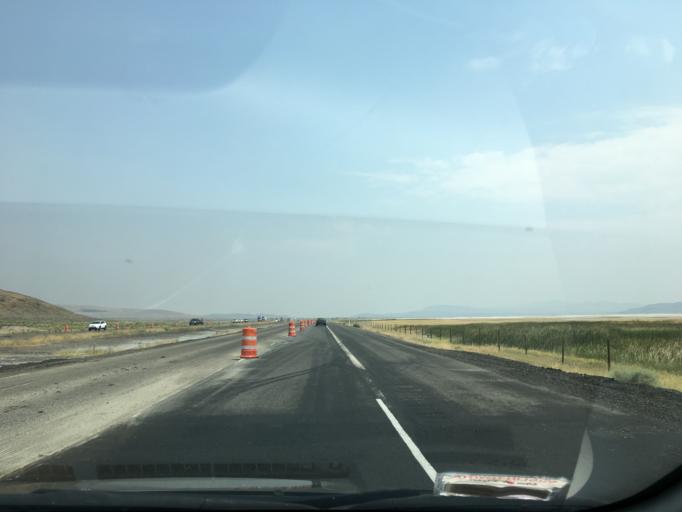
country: US
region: Nevada
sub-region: Lyon County
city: Fernley
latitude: 39.6993
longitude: -119.1020
